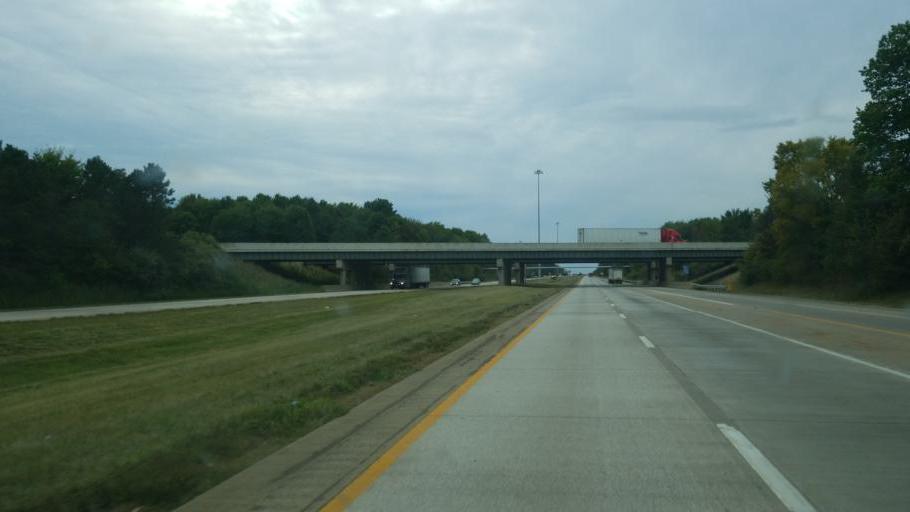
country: US
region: Ohio
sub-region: Trumbull County
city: Lordstown
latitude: 41.1102
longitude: -80.8361
